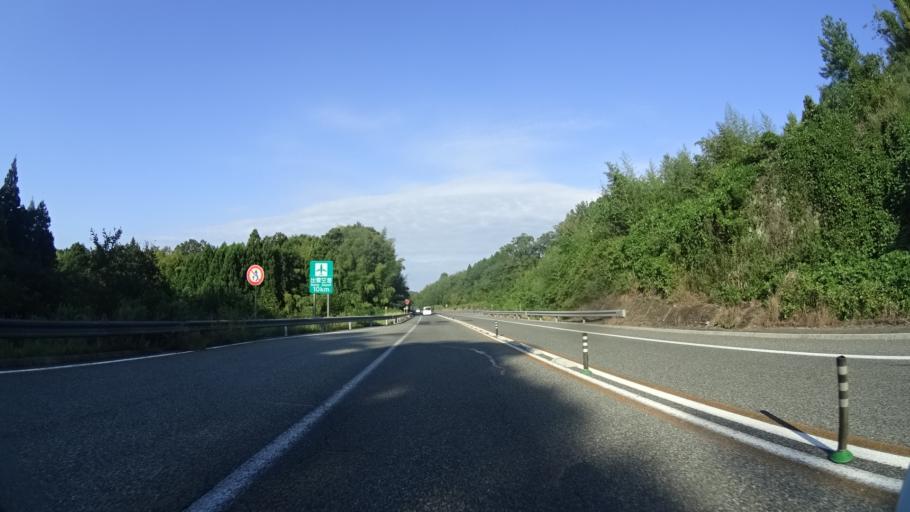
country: JP
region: Shimane
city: Matsue-shi
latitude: 35.4119
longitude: 132.9540
